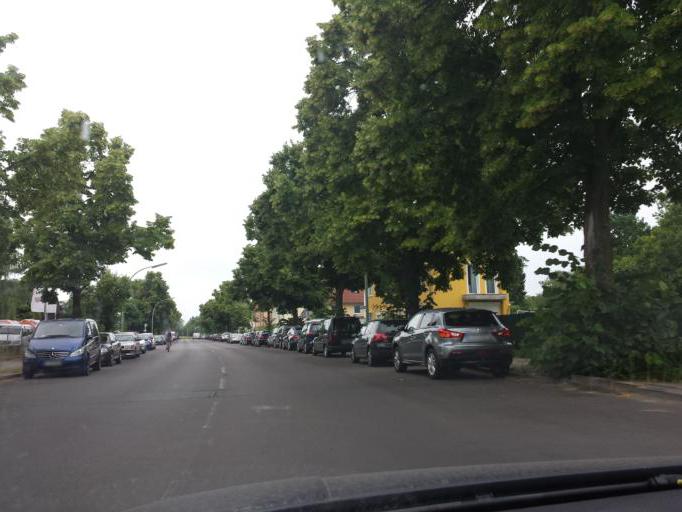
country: DE
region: Berlin
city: Marienfelde
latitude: 52.4131
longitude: 13.3783
